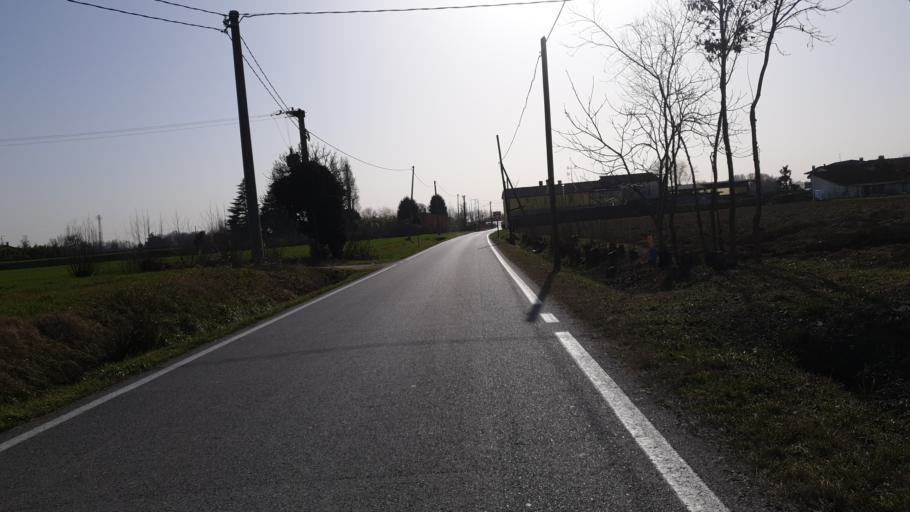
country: IT
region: Veneto
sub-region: Provincia di Padova
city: Tavo
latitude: 45.4877
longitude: 11.8802
